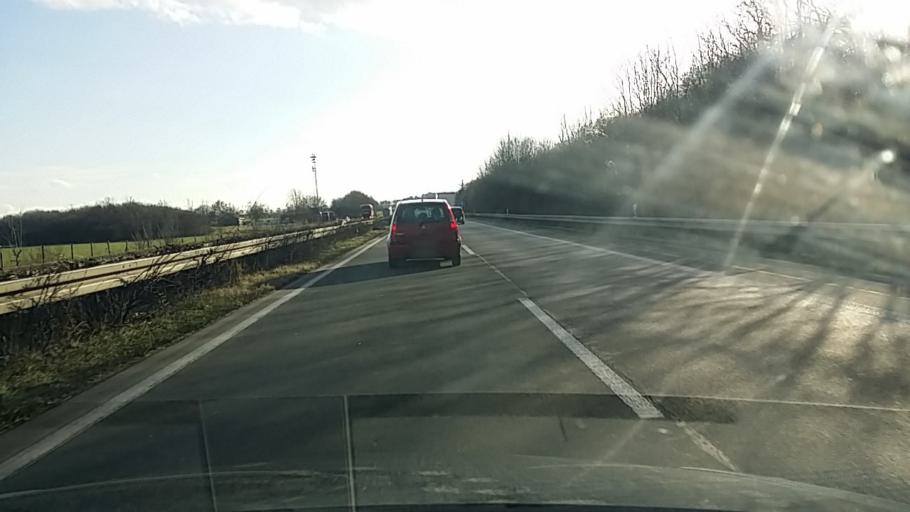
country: DE
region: North Rhine-Westphalia
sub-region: Regierungsbezirk Detmold
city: Paderborn
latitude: 51.6322
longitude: 8.7225
